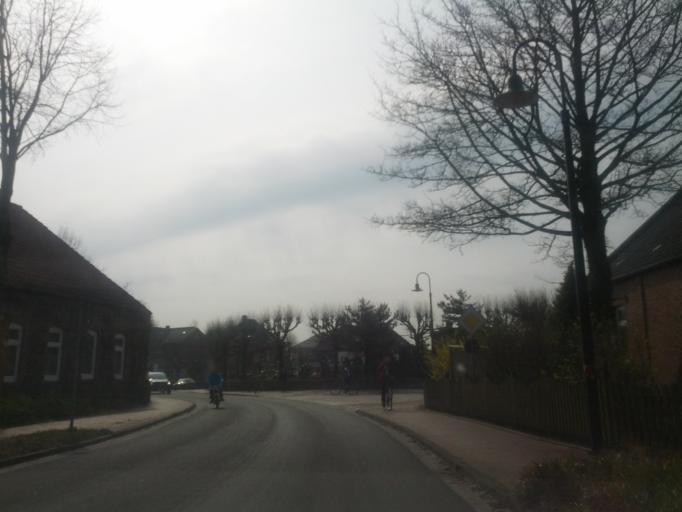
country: DE
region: Lower Saxony
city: Marienhafe
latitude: 53.5238
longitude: 7.2731
